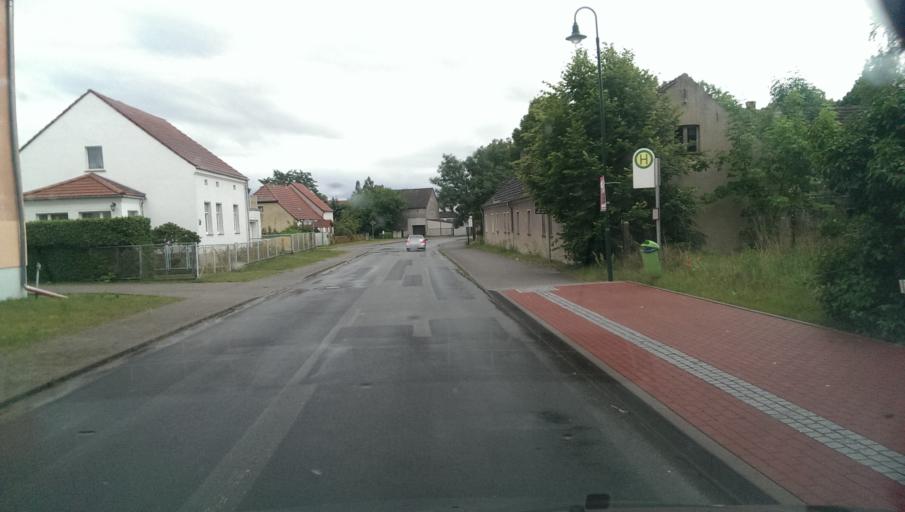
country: DE
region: Brandenburg
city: Gross Kreutz
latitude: 52.3678
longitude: 12.7173
